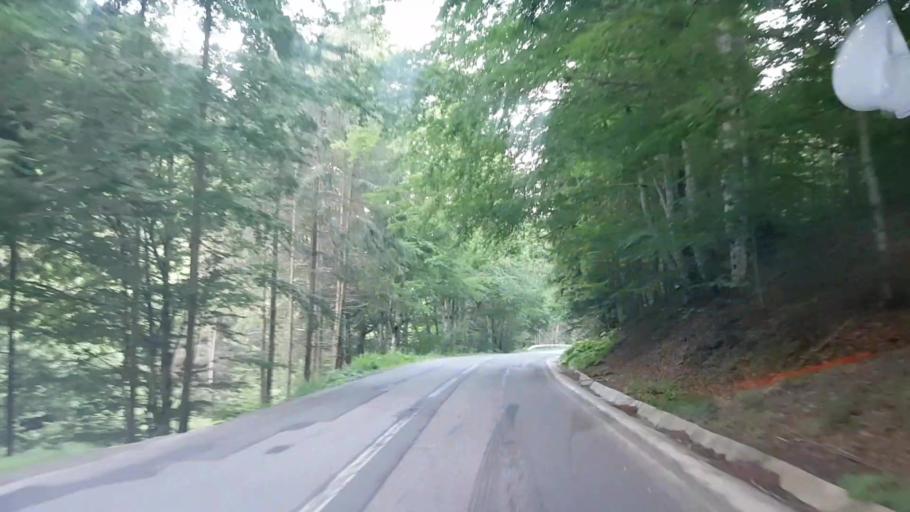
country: RO
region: Harghita
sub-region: Comuna Praid
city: Ocna de Sus
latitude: 46.6019
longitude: 25.2391
